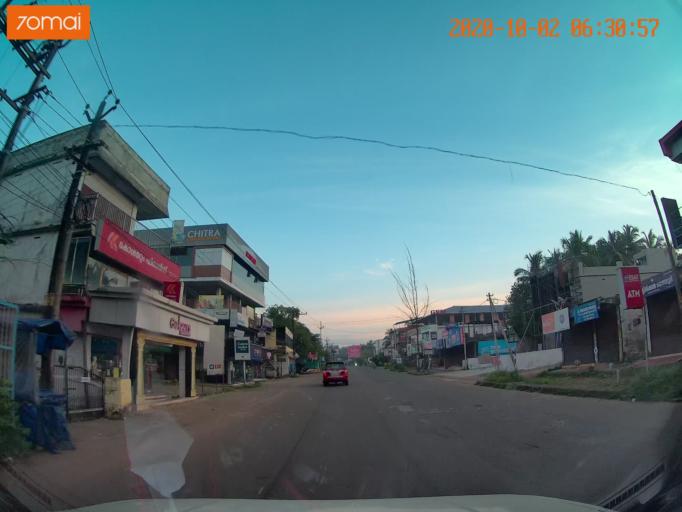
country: IN
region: Kerala
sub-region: Thrissur District
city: Kunnamkulam
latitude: 10.7372
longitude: 76.0289
